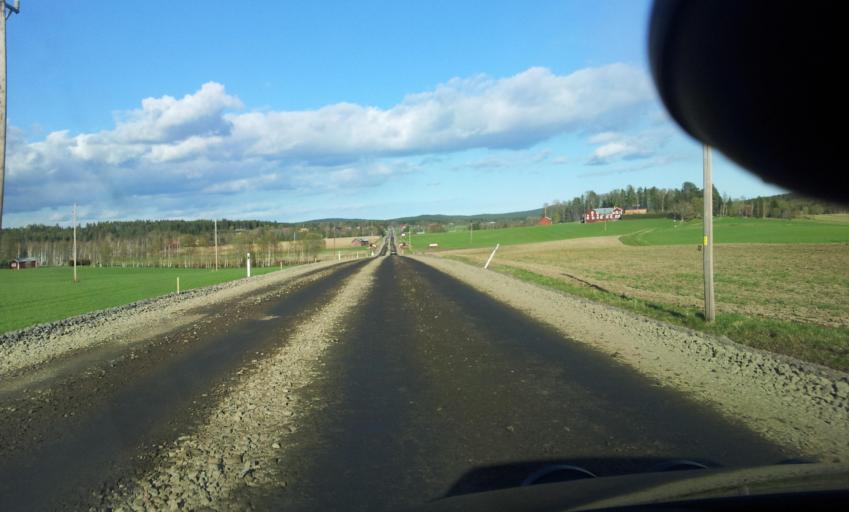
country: SE
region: Gaevleborg
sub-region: Bollnas Kommun
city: Kilafors
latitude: 61.3502
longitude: 16.6530
